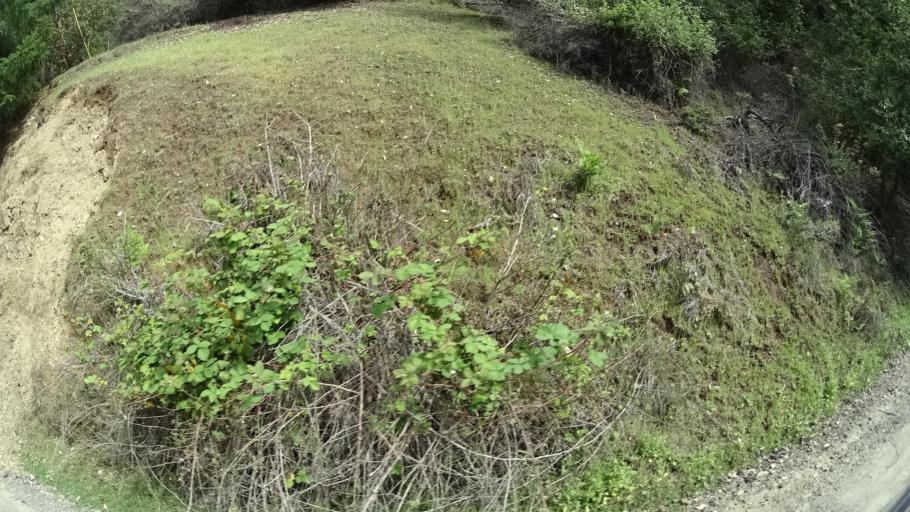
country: US
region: California
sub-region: Humboldt County
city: Redway
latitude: 40.0392
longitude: -123.8436
